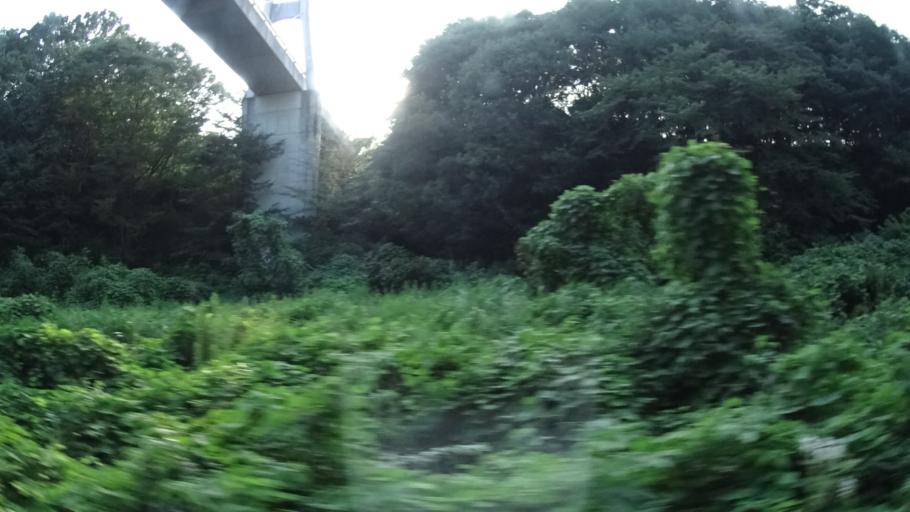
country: JP
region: Tochigi
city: Karasuyama
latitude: 36.6106
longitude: 140.1538
